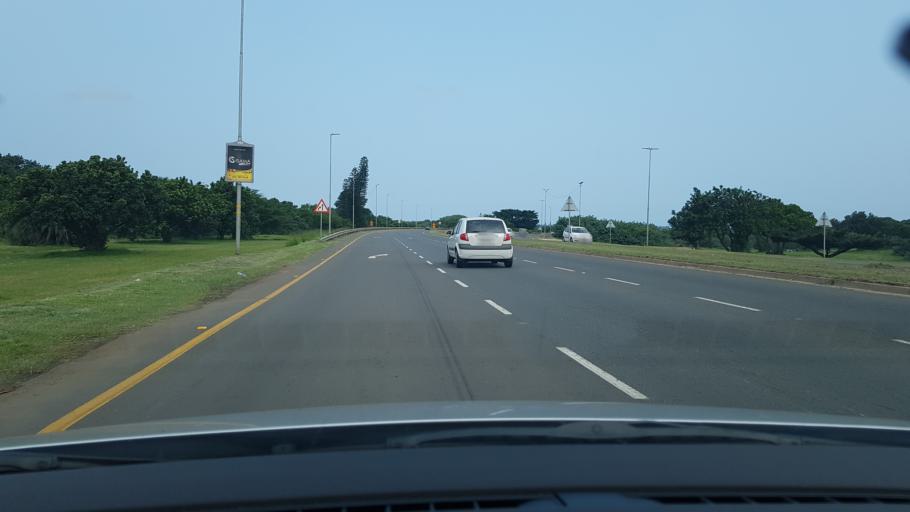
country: ZA
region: KwaZulu-Natal
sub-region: uThungulu District Municipality
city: Richards Bay
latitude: -28.7724
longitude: 32.0693
